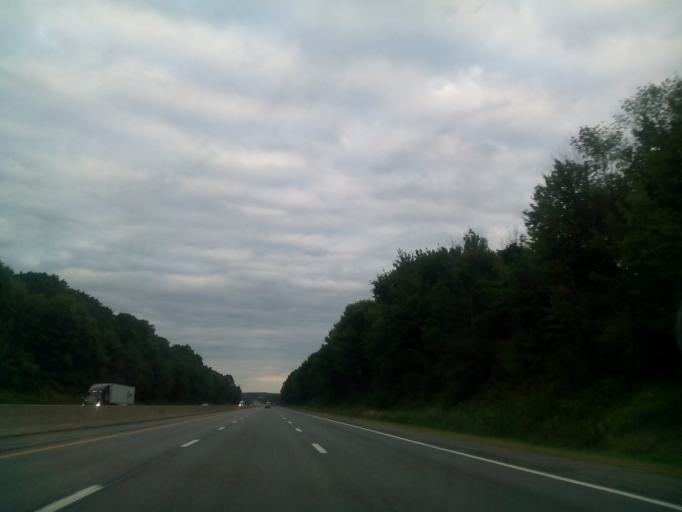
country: US
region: Ohio
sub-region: Portage County
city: Windham
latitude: 41.2435
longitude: -81.0812
